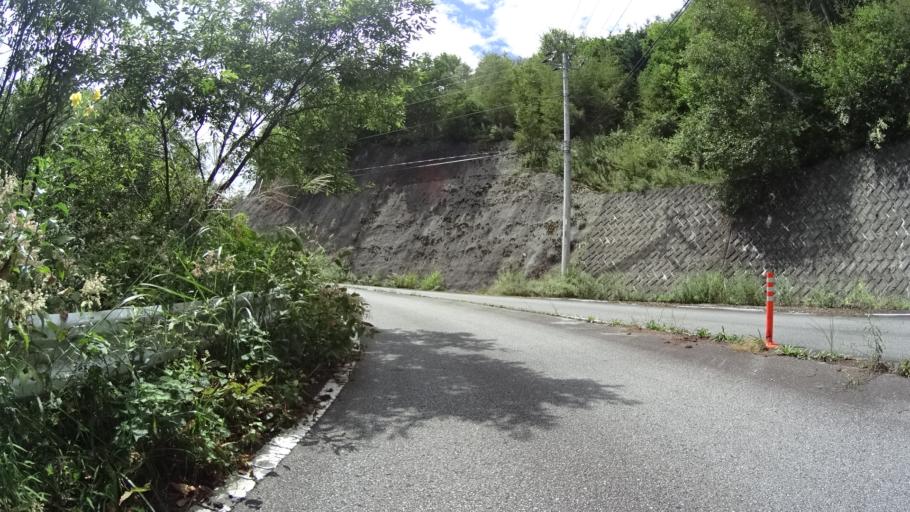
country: JP
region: Yamanashi
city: Enzan
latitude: 35.8020
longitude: 138.6522
